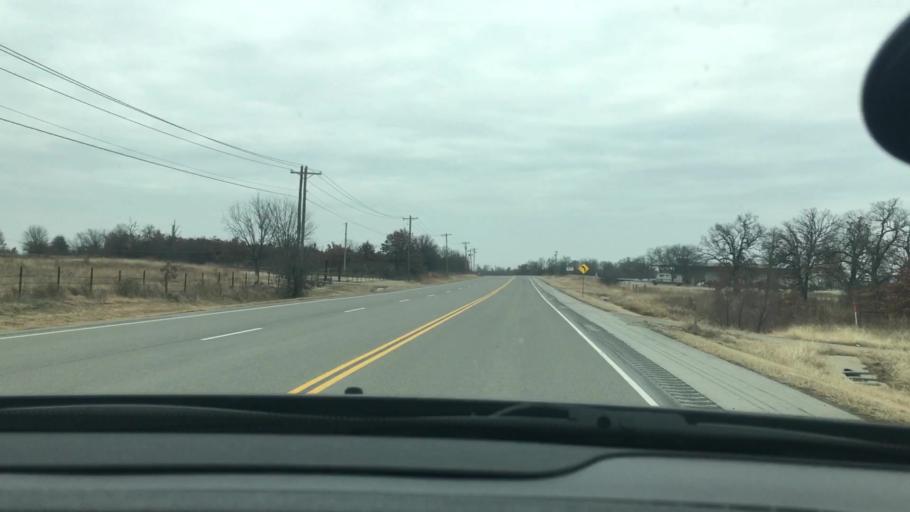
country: US
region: Oklahoma
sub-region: Carter County
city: Healdton
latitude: 34.3953
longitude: -97.5031
